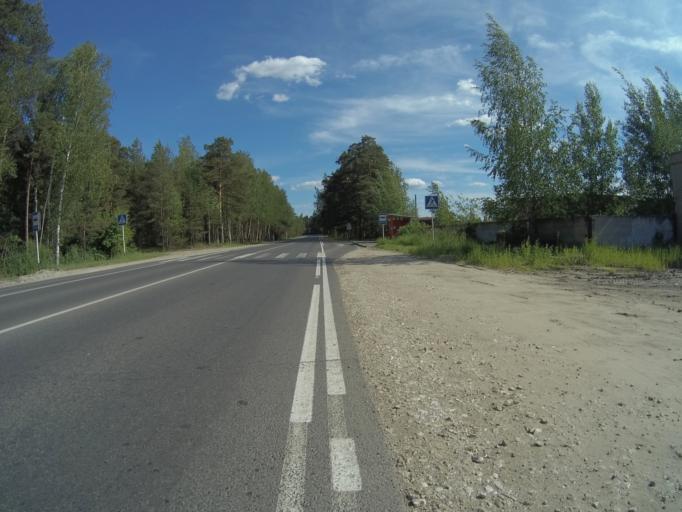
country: RU
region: Vladimir
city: Raduzhnyy
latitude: 56.0259
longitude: 40.3804
